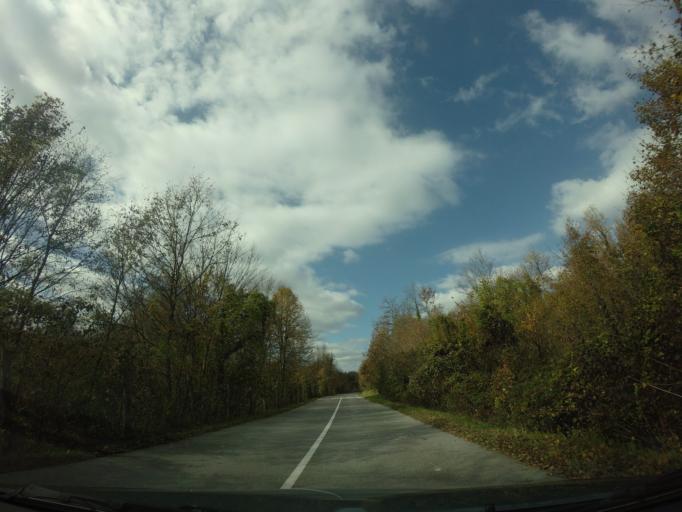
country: HR
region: Karlovacka
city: Plaski
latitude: 45.1897
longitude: 15.4437
